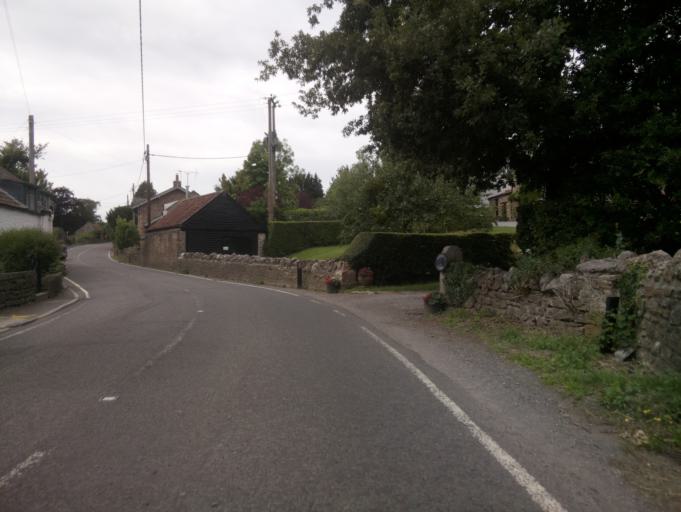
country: GB
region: England
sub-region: Somerset
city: Bradley Cross
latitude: 51.2484
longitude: -2.7374
